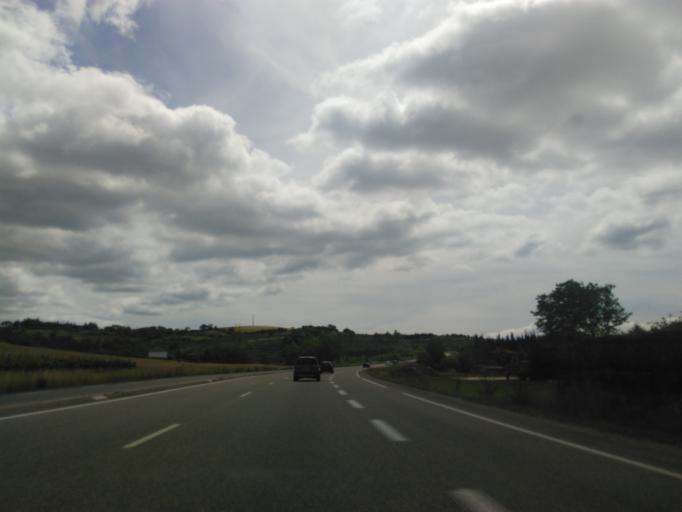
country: FR
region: Rhone-Alpes
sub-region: Departement de l'Ardeche
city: Villeneuve-de-Berg
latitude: 44.5856
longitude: 4.5338
